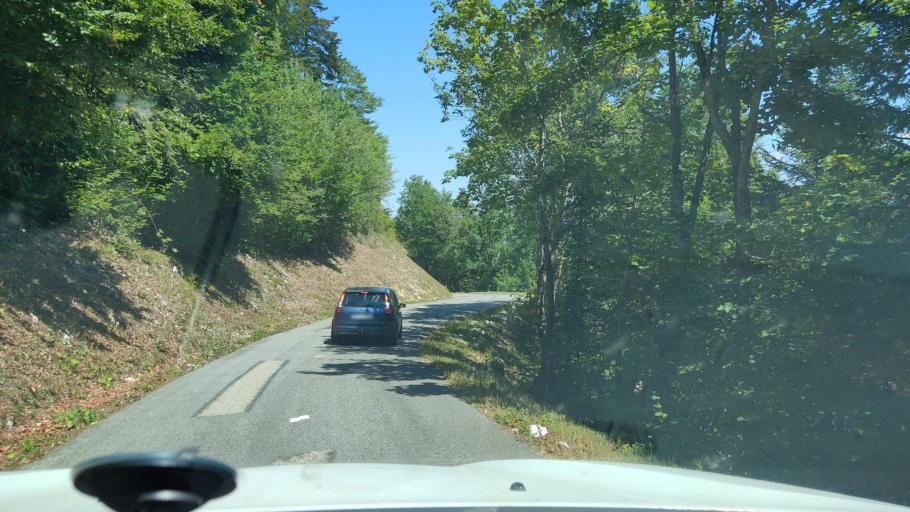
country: FR
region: Rhone-Alpes
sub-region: Departement de la Savoie
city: Le Bourget-du-Lac
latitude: 45.6567
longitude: 5.8317
